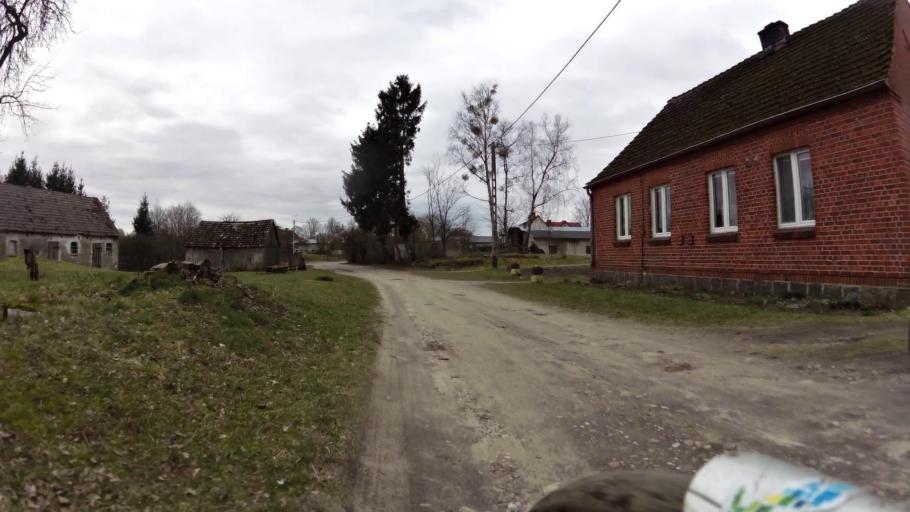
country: PL
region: Pomeranian Voivodeship
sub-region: Powiat bytowski
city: Trzebielino
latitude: 54.1072
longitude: 17.1300
